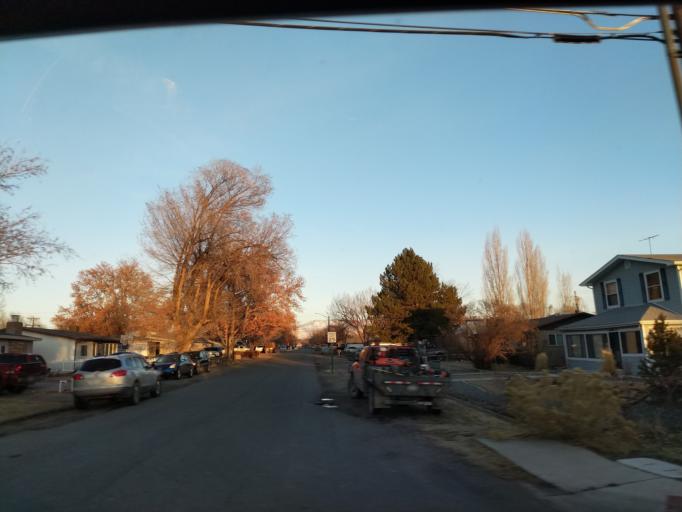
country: US
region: Colorado
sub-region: Mesa County
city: Grand Junction
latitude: 39.0936
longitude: -108.5523
